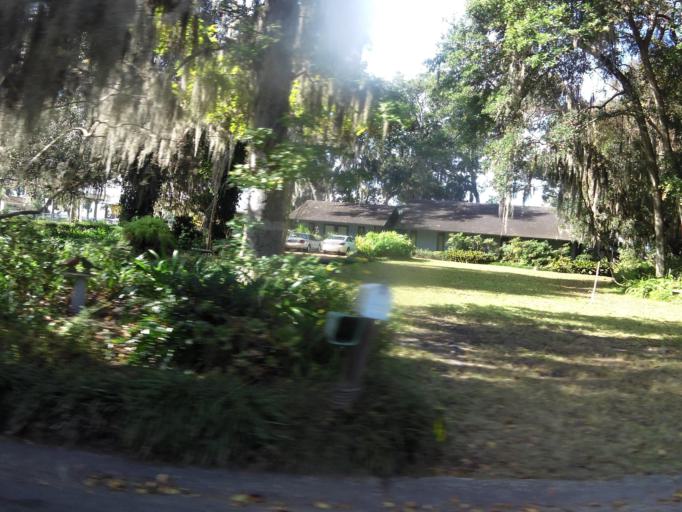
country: US
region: Georgia
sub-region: Glynn County
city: Brunswick
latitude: 31.1238
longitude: -81.5564
